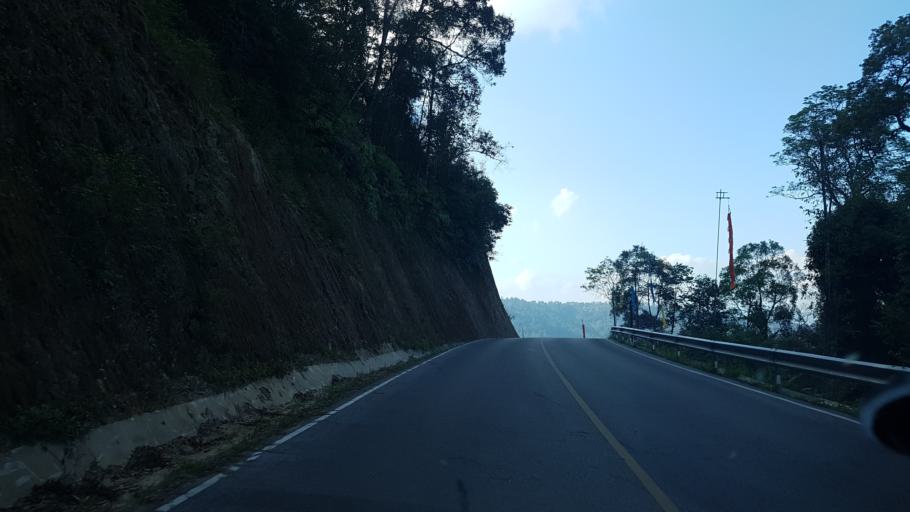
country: TH
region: Chiang Rai
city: Mae Fa Luang
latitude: 20.3267
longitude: 99.8305
